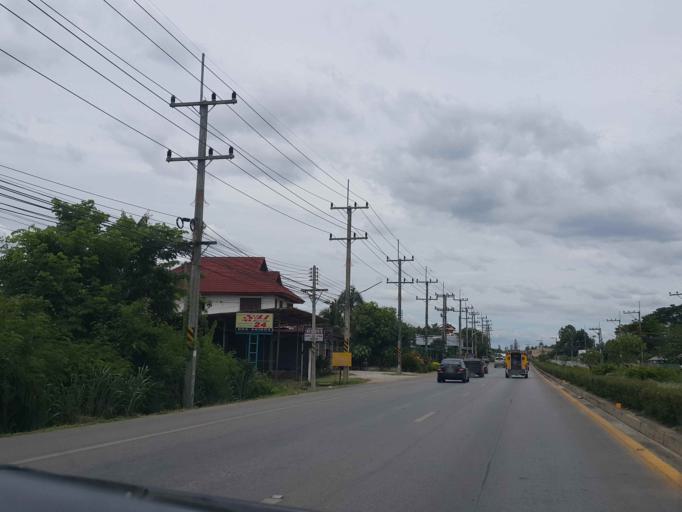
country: TH
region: Chiang Mai
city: San Pa Tong
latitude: 18.5885
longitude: 98.8877
